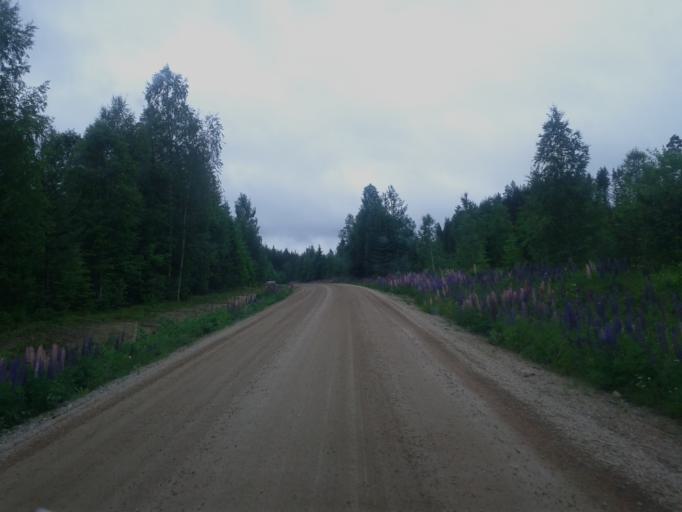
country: SE
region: Gaevleborg
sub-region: Hudiksvalls Kommun
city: Delsbo
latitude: 62.1320
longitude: 16.6457
